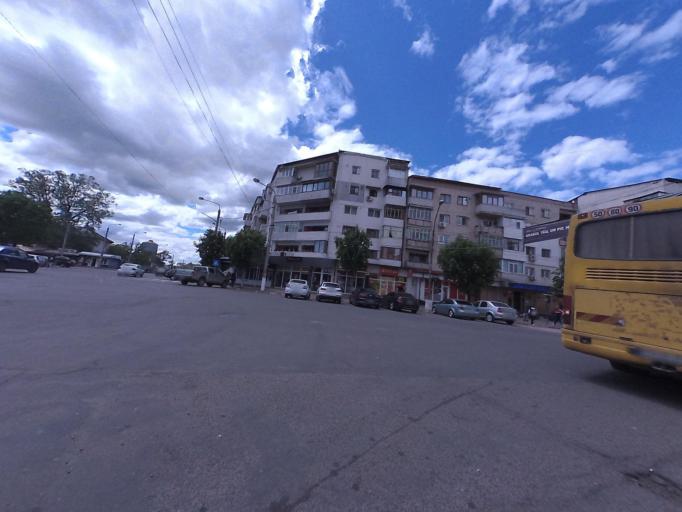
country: RO
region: Vaslui
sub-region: Municipiul Barlad
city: Barlad
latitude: 46.2159
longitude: 27.6726
